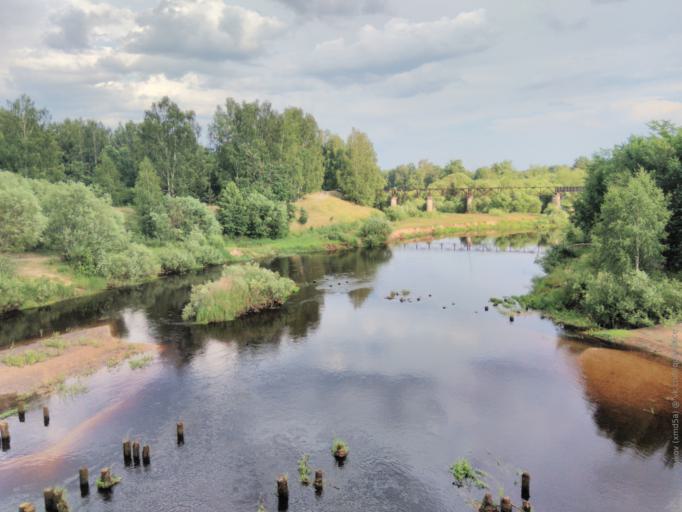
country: RU
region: Ivanovo
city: Talitsy
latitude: 56.5311
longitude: 42.3426
